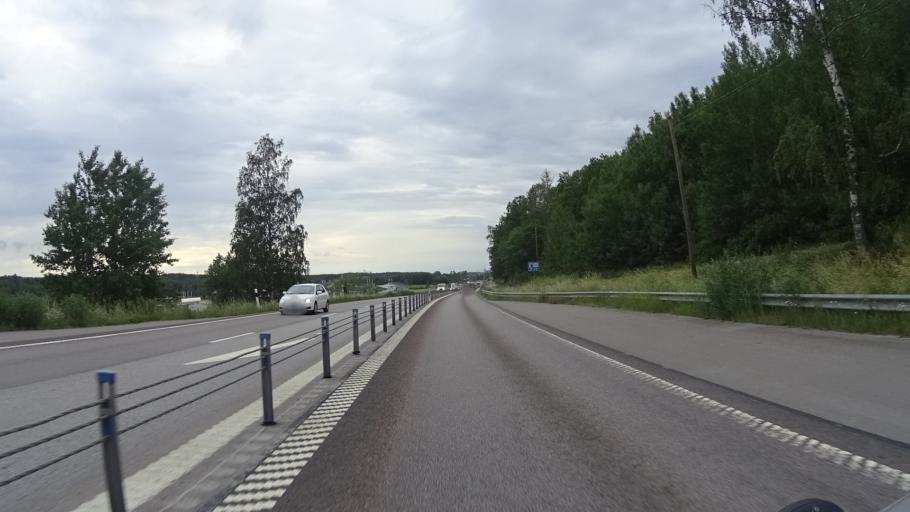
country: SE
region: OEstergoetland
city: Lindo
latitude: 58.5530
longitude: 16.2418
